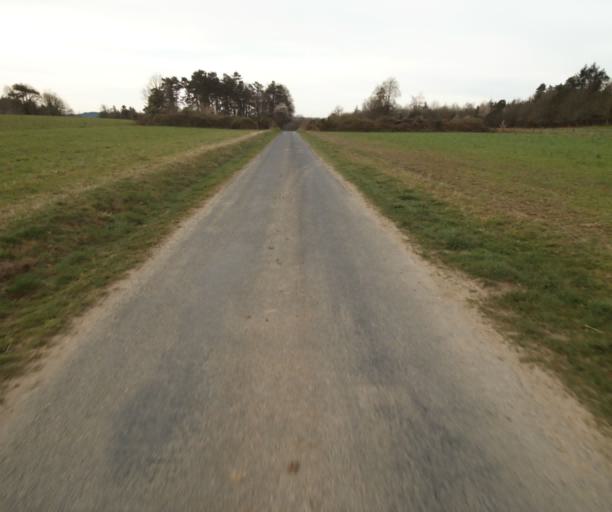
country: FR
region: Limousin
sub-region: Departement de la Correze
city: Correze
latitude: 45.4447
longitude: 1.8208
